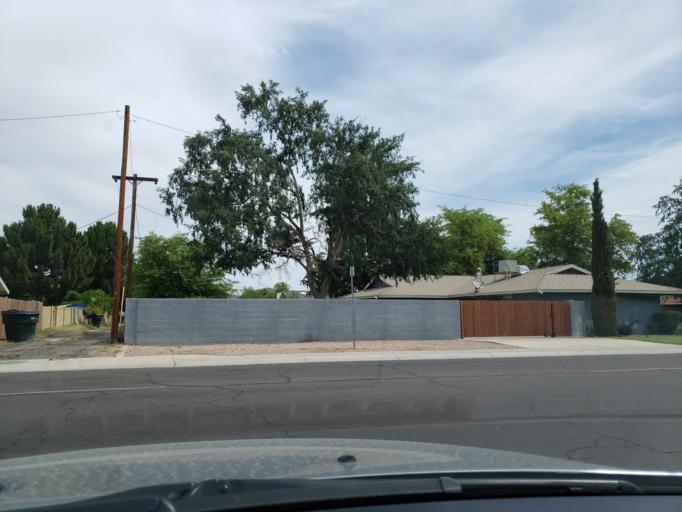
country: US
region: Arizona
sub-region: Maricopa County
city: Glendale
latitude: 33.5457
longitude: -112.0976
